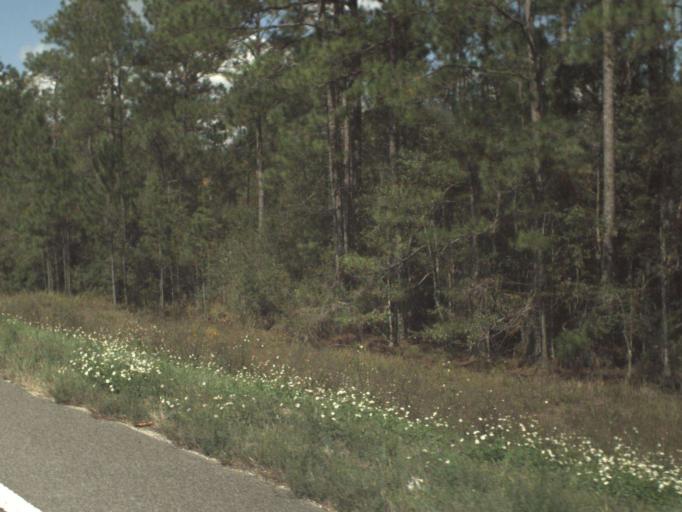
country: US
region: Florida
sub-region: Walton County
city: Freeport
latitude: 30.4596
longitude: -85.9240
